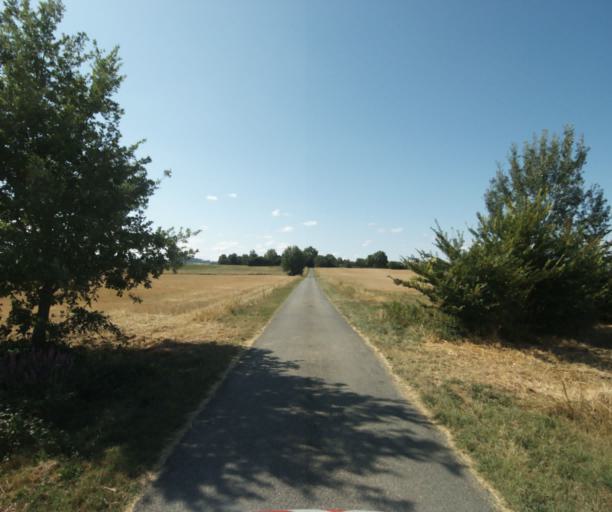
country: FR
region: Midi-Pyrenees
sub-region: Departement de la Haute-Garonne
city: Revel
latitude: 43.4971
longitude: 1.9836
